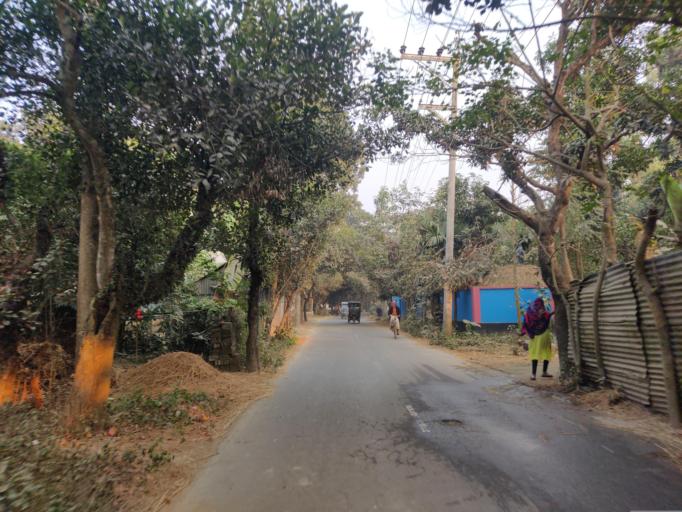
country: BD
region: Dhaka
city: Bajitpur
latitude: 24.1581
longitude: 90.7606
